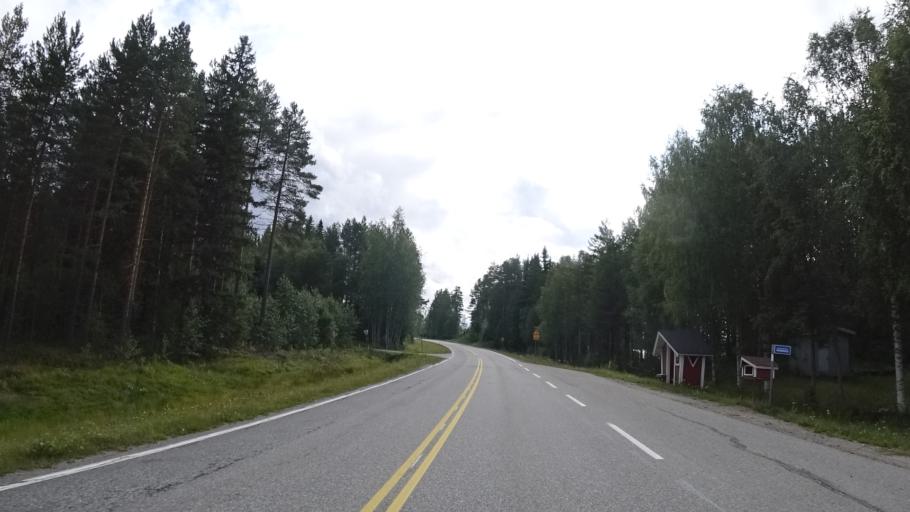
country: FI
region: North Karelia
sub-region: Joensuu
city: Ilomantsi
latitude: 62.7527
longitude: 30.9977
